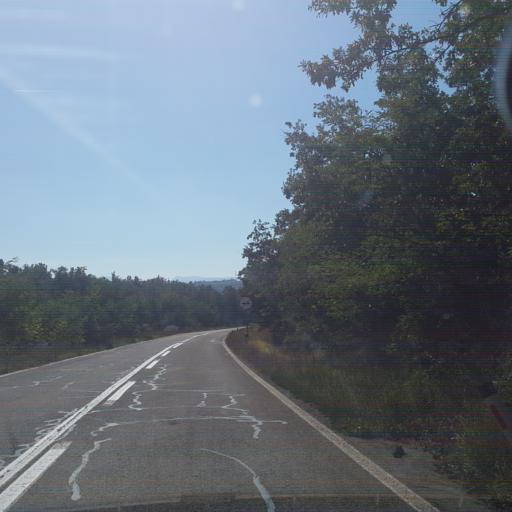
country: RS
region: Central Serbia
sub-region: Nisavski Okrug
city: Svrljig
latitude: 43.4603
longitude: 22.2080
